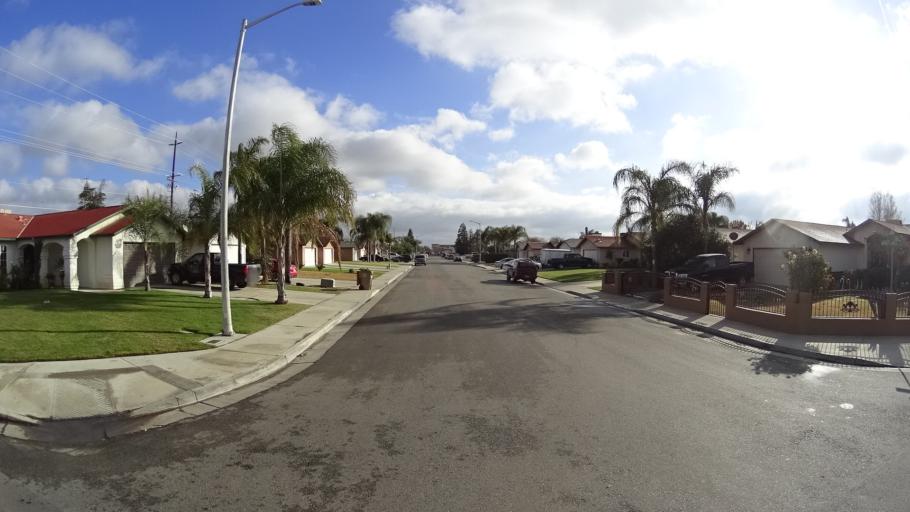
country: US
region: California
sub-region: Kern County
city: Greenfield
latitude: 35.2954
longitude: -119.0075
